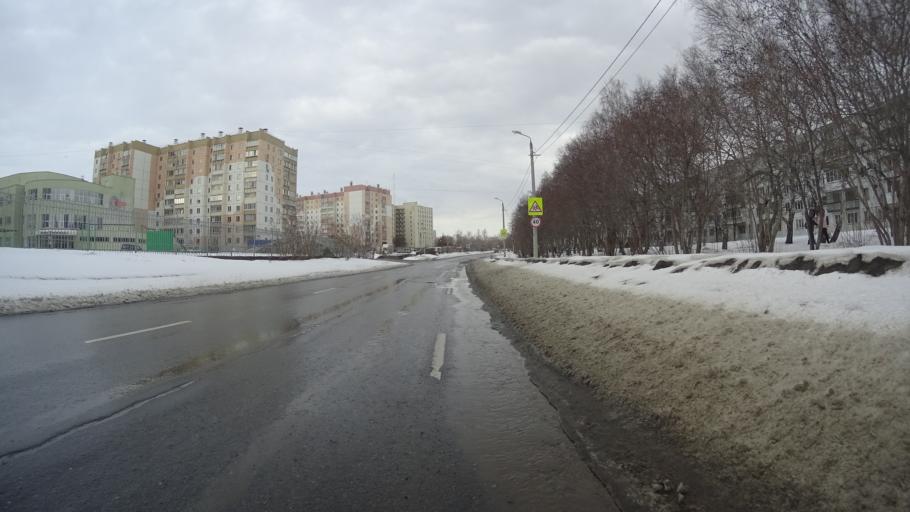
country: RU
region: Chelyabinsk
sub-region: Gorod Chelyabinsk
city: Chelyabinsk
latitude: 55.1982
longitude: 61.3217
